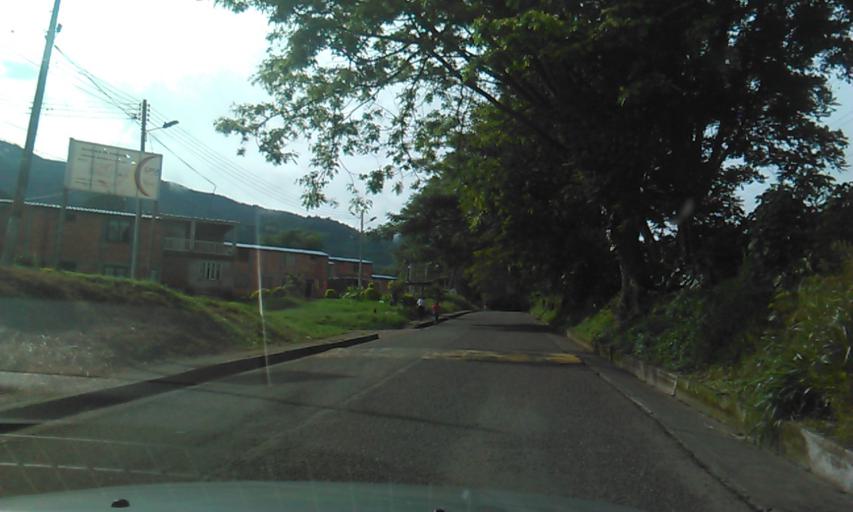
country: CO
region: Quindio
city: Cordoba
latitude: 4.3974
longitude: -75.6895
